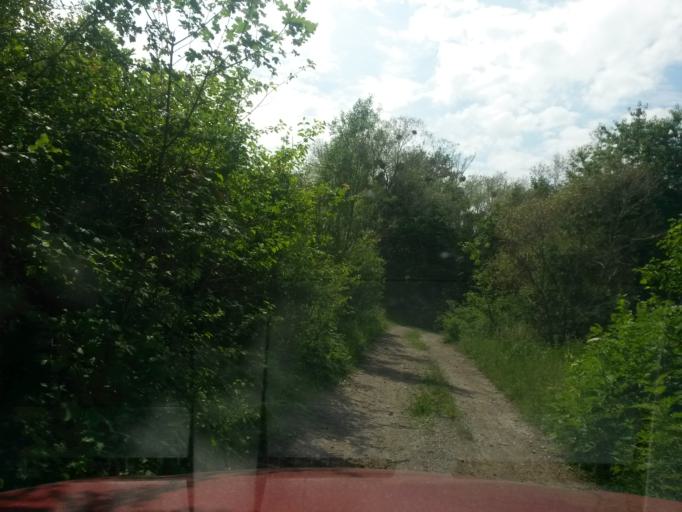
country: SK
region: Kosicky
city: Secovce
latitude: 48.6283
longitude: 21.4900
